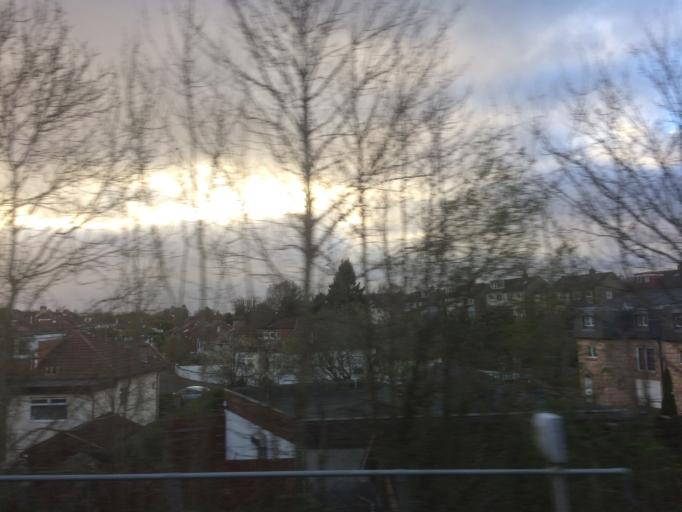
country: GB
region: Scotland
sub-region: East Renfrewshire
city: Giffnock
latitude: 55.8124
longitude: -4.2716
